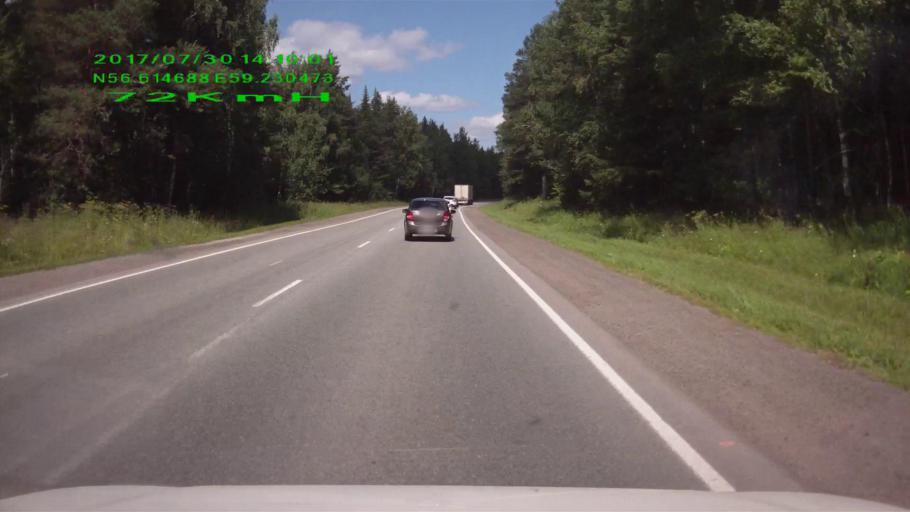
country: RU
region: Sverdlovsk
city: Nizhniye Sergi
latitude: 56.6149
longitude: 59.2306
